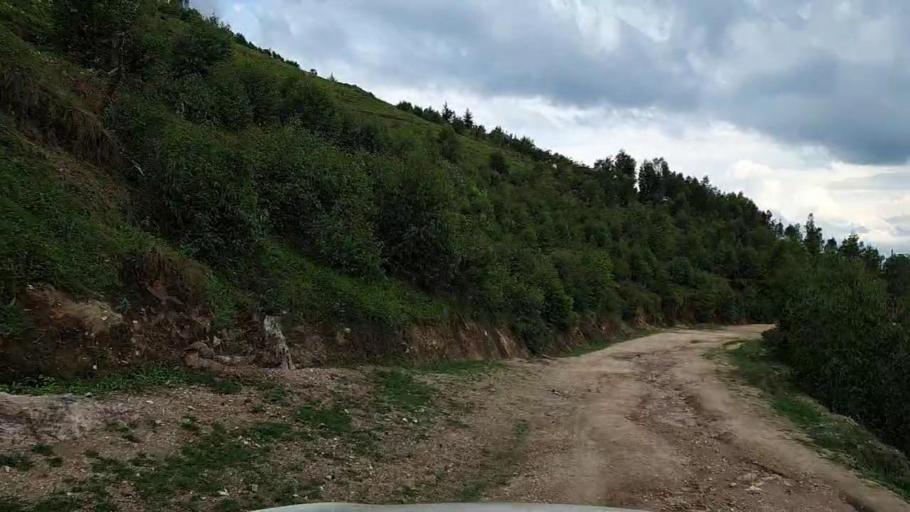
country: RW
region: Southern Province
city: Gikongoro
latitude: -2.4361
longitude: 29.6334
